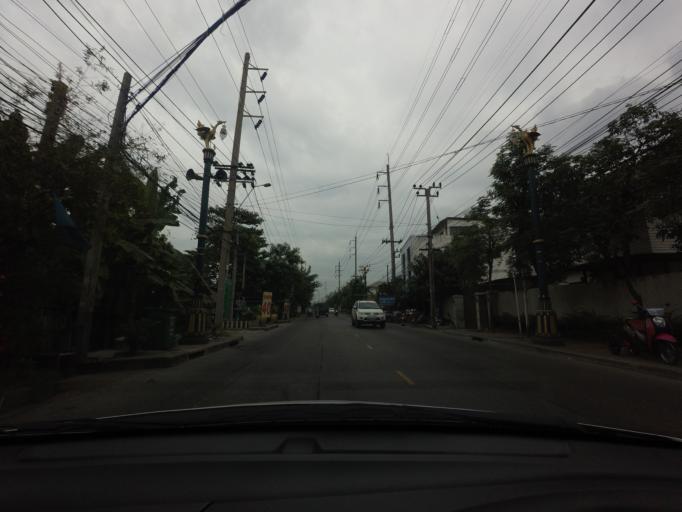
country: TH
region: Samut Prakan
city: Phra Pradaeng
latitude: 13.6652
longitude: 100.5417
